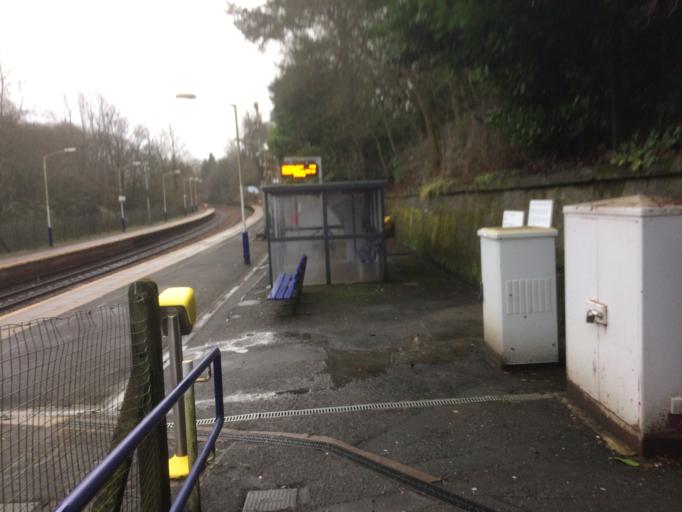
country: GB
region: Scotland
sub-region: East Renfrewshire
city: Giffnock
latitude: 55.8110
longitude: -4.3117
